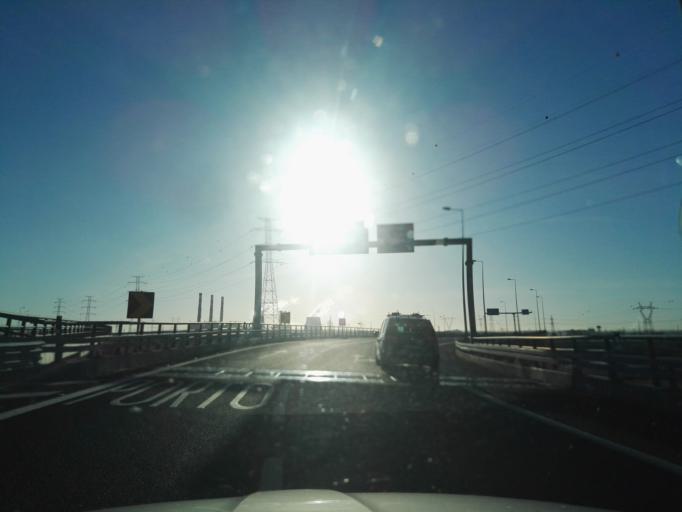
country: PT
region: Lisbon
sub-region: Alenquer
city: Carregado
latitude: 39.0173
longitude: -8.9701
